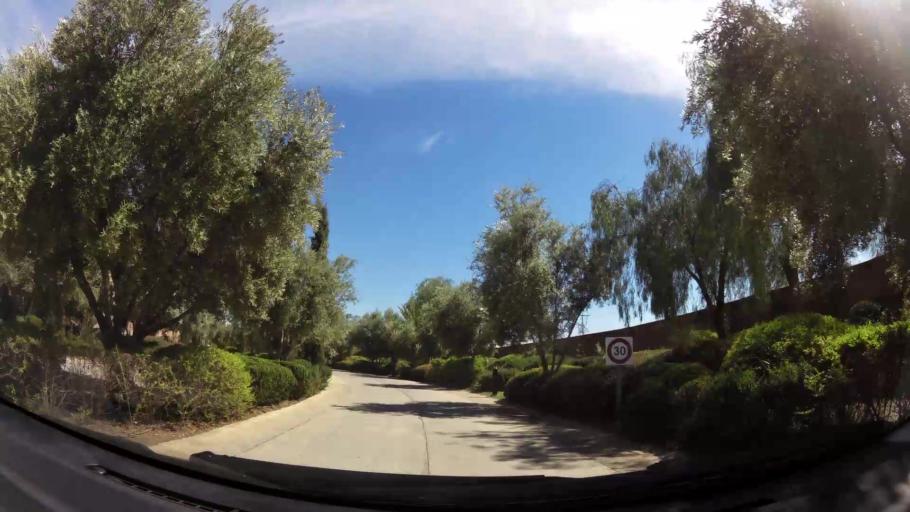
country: MA
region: Marrakech-Tensift-Al Haouz
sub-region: Marrakech
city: Marrakesh
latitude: 31.6044
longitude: -7.9544
